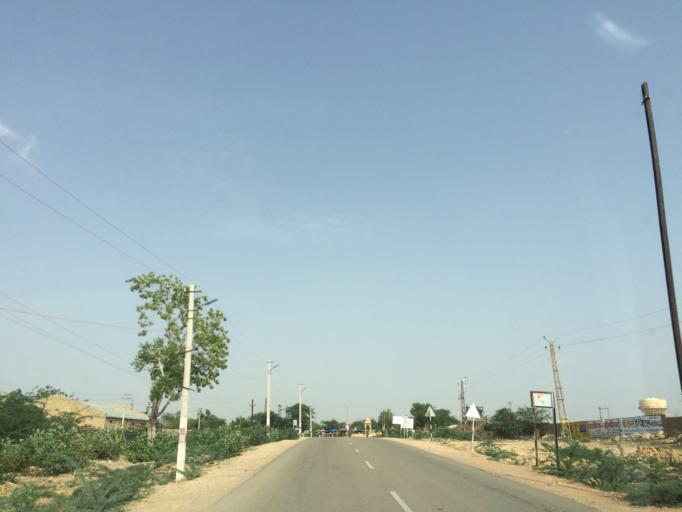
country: IN
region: Rajasthan
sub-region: Jaisalmer
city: Jaisalmer
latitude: 26.9102
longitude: 70.9368
